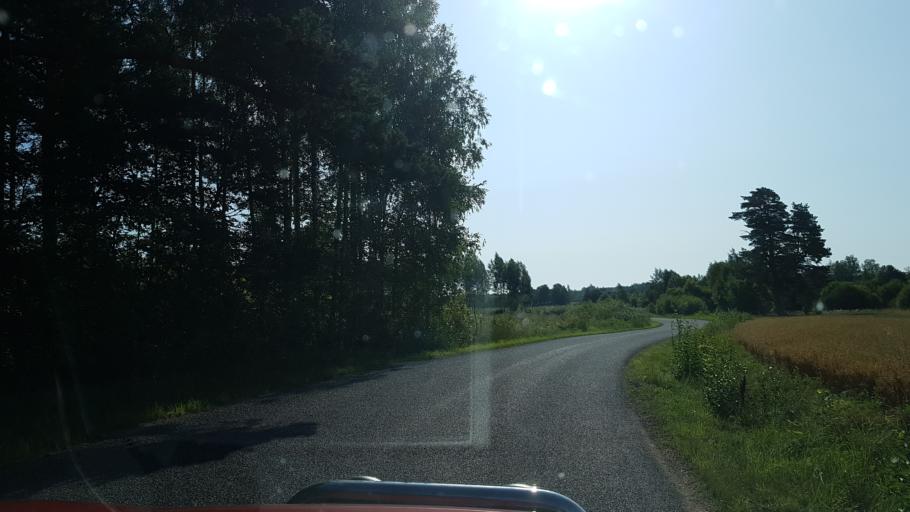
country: LV
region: Apes Novads
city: Ape
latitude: 57.6562
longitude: 26.7320
